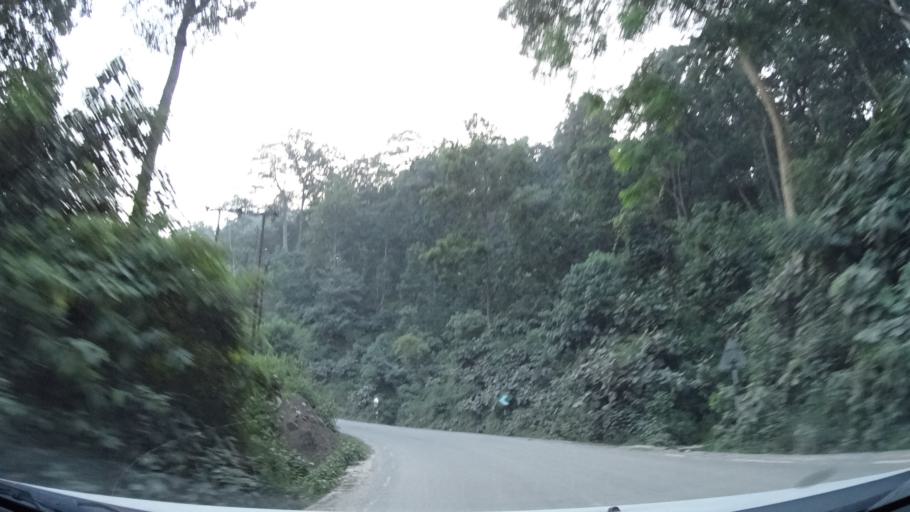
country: IN
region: Uttar Pradesh
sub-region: Maharajganj
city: Nichlaul
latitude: 27.5583
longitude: 83.8445
